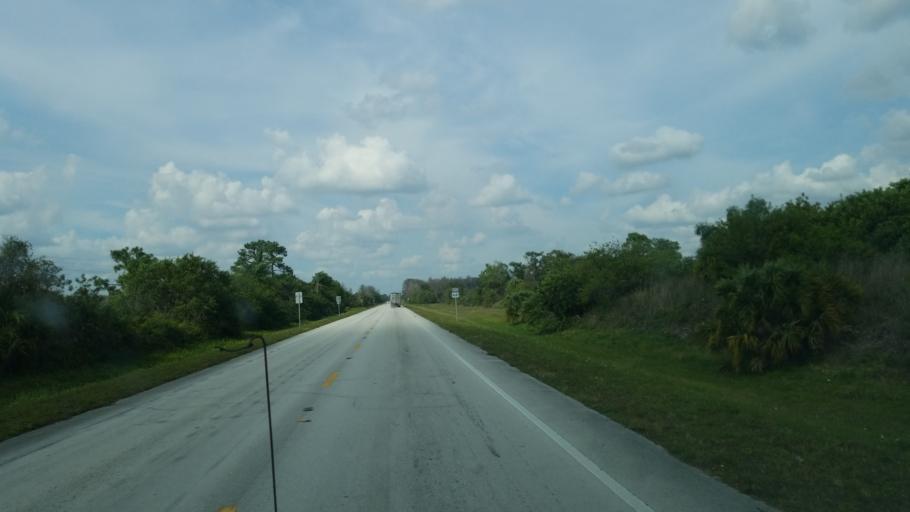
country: US
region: Florida
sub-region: Indian River County
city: Fellsmere
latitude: 27.7017
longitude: -80.9053
